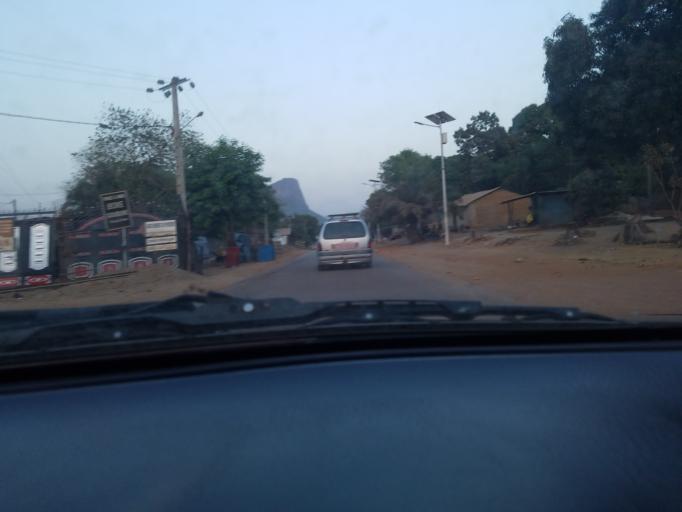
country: GN
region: Kindia
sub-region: Prefecture de Dubreka
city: Dubreka
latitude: 9.7892
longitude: -13.5049
